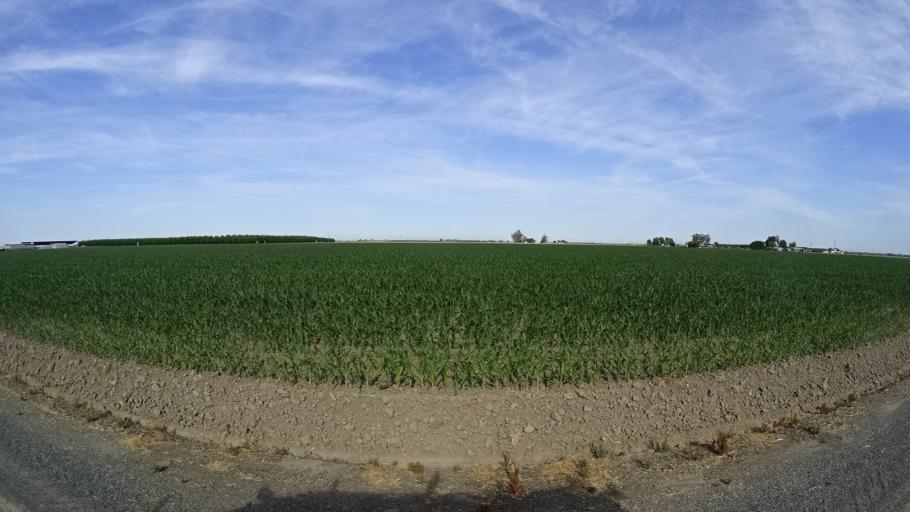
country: US
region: California
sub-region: Kings County
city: Hanford
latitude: 36.3695
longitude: -119.5470
